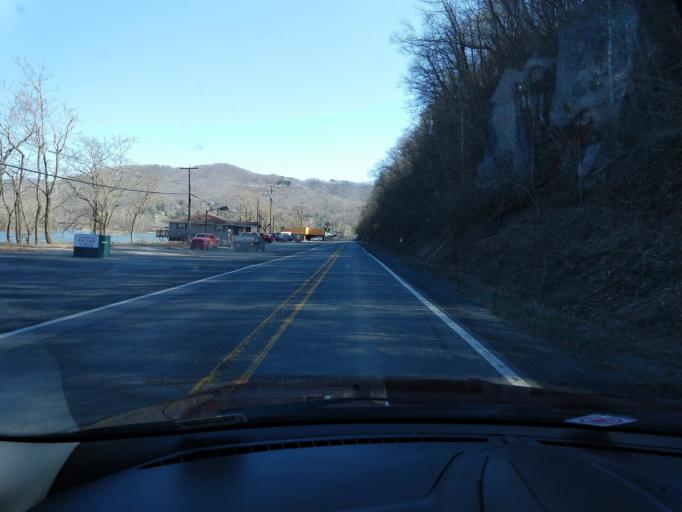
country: US
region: West Virginia
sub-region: Summers County
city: Hinton
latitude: 37.6545
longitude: -80.8928
